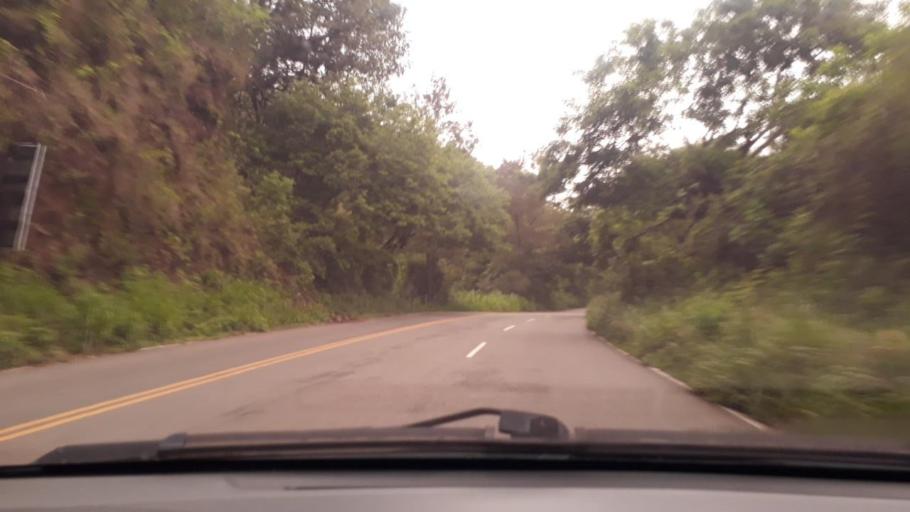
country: GT
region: Chiquimula
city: Esquipulas
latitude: 14.5542
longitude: -89.3815
